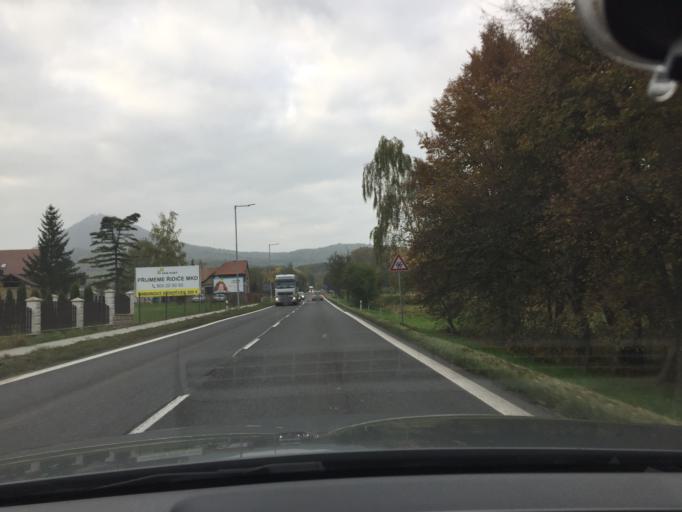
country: CZ
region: Ustecky
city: Velemin
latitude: 50.5439
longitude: 13.9742
